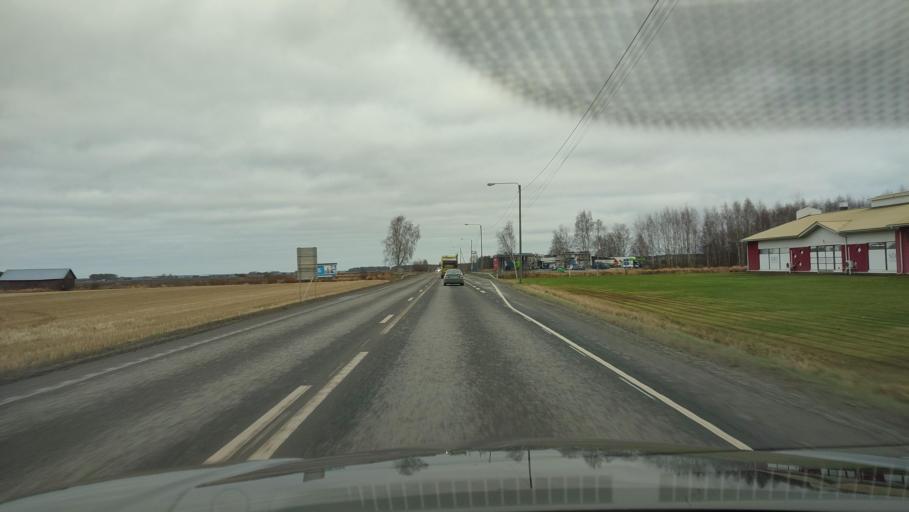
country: FI
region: Southern Ostrobothnia
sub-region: Seinaejoki
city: Ilmajoki
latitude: 62.7320
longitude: 22.6021
